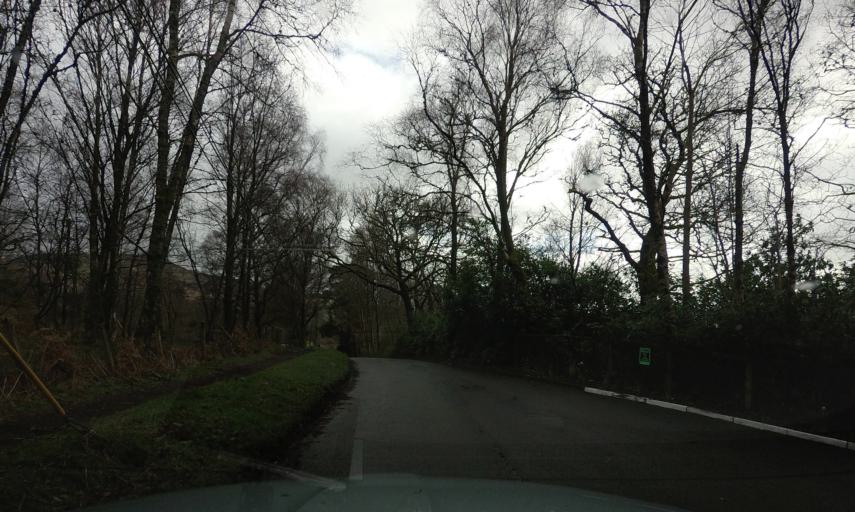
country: GB
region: Scotland
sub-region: West Dunbartonshire
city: Balloch
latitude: 56.1004
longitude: -4.5614
